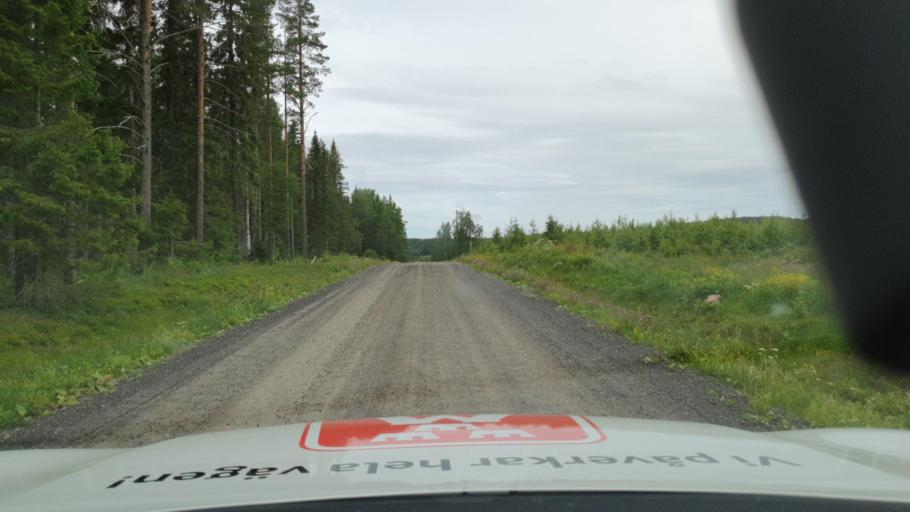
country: SE
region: Vaesterbotten
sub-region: Skelleftea Kommun
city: Burtraesk
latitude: 64.3862
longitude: 20.6133
